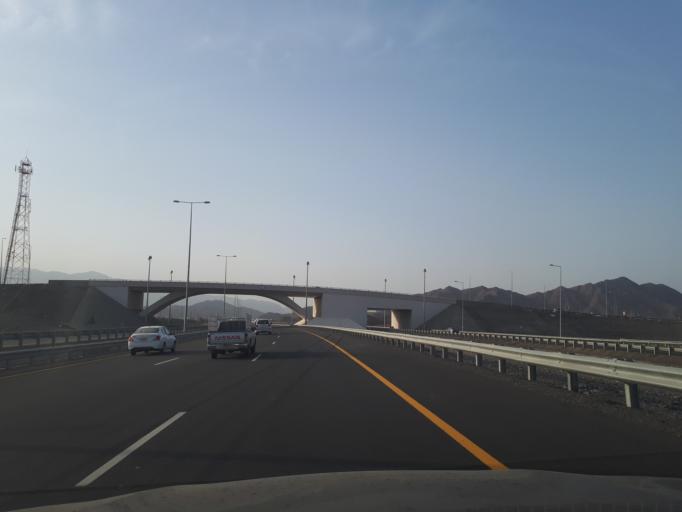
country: OM
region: Muhafazat ad Dakhiliyah
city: Bidbid
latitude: 23.3273
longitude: 58.1157
